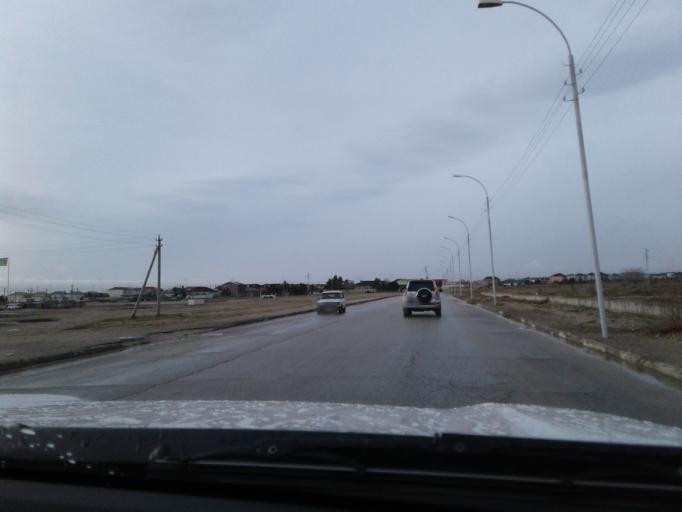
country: TM
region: Balkan
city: Balkanabat
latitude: 39.5295
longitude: 54.3581
